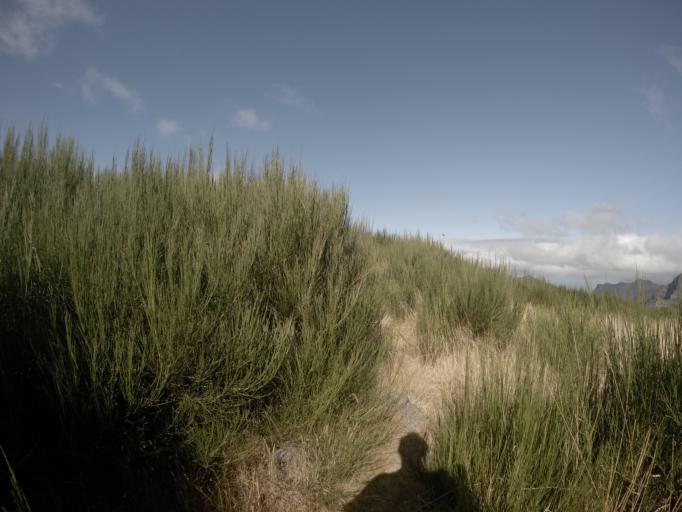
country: PT
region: Madeira
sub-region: Camara de Lobos
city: Curral das Freiras
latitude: 32.7150
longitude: -16.9918
